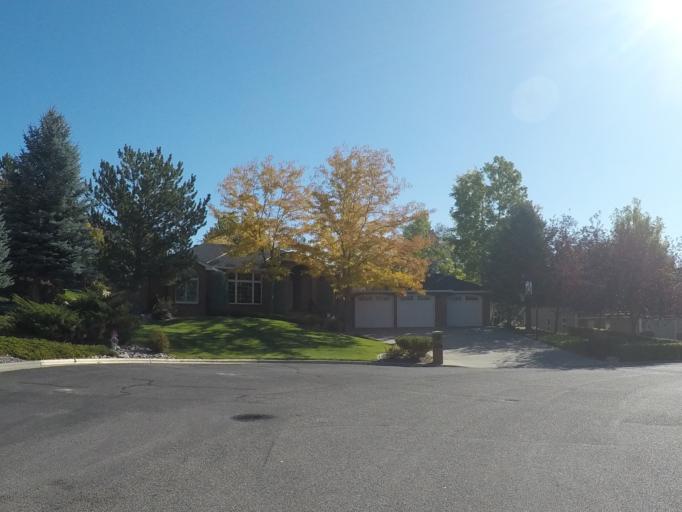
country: US
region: Montana
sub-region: Yellowstone County
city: Billings
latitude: 45.8013
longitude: -108.5891
